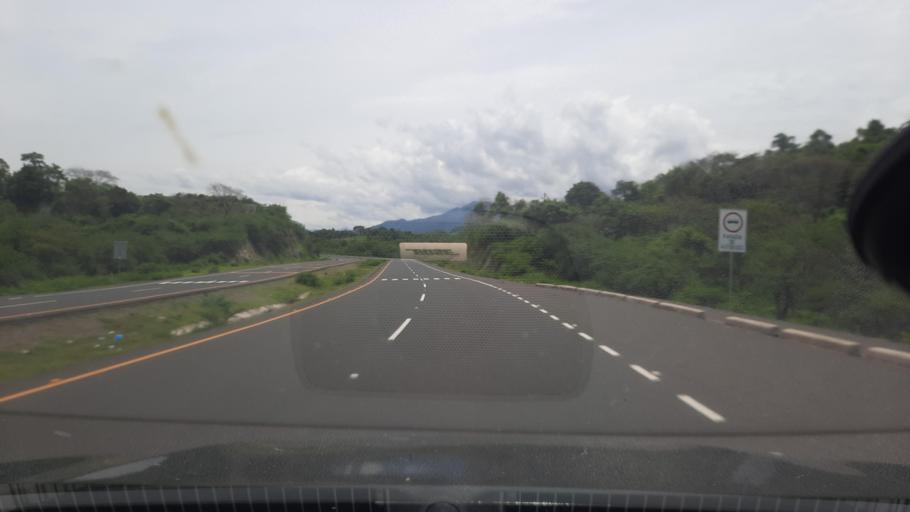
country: HN
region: Valle
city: Aramecina
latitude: 13.7097
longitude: -87.7074
